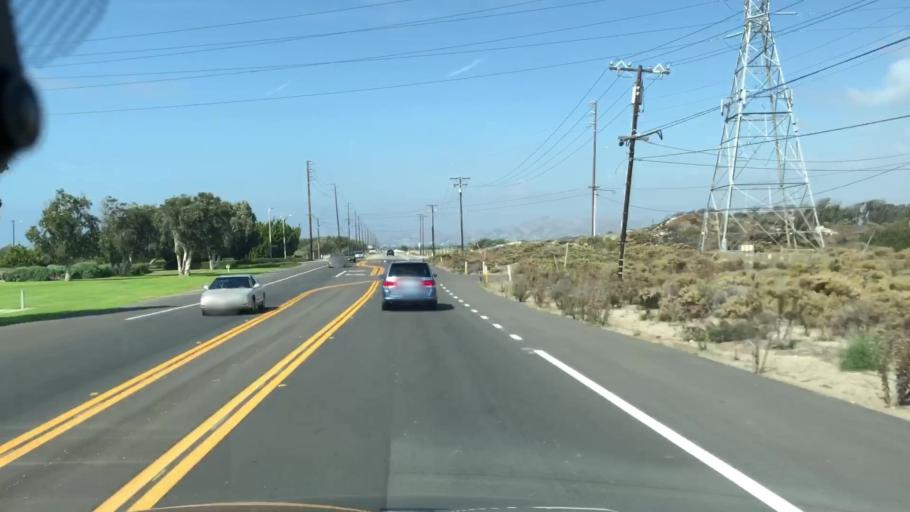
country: US
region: California
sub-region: Ventura County
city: Oxnard Shores
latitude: 34.2075
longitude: -119.2477
